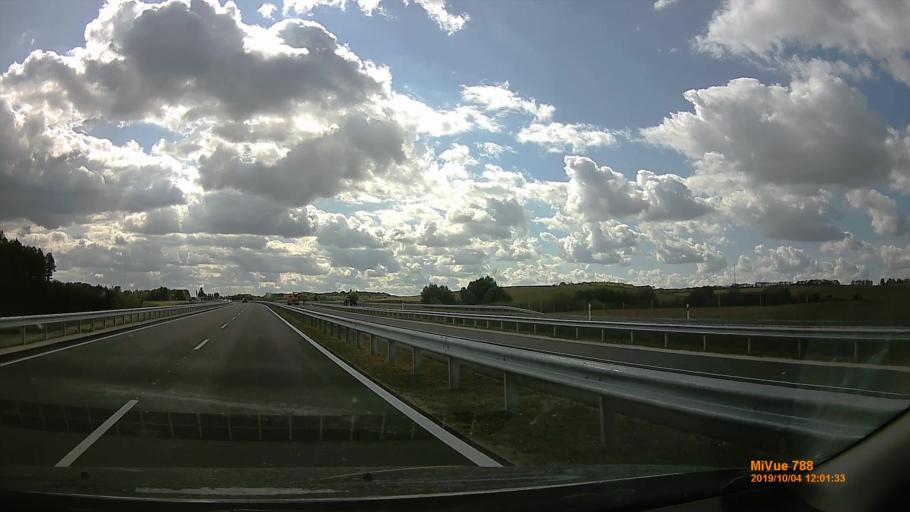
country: HU
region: Somogy
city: Karad
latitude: 46.6111
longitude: 17.7977
